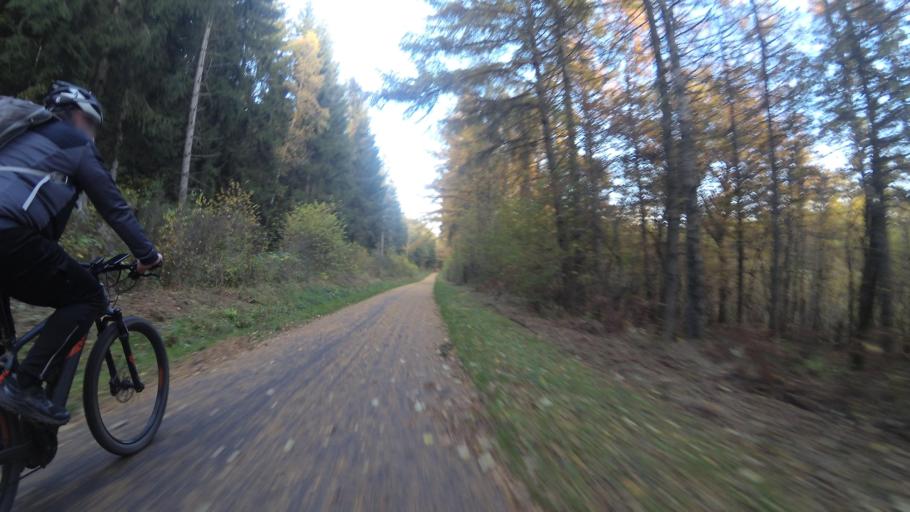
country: DE
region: Rheinland-Pfalz
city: Mandern
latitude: 49.6135
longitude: 6.7542
